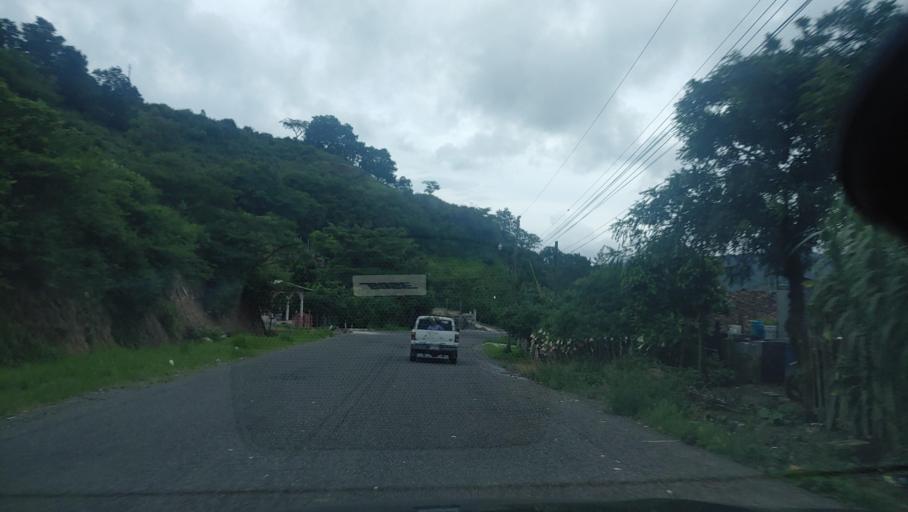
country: HN
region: Choluteca
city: San Marcos de Colon
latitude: 13.3760
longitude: -86.8913
